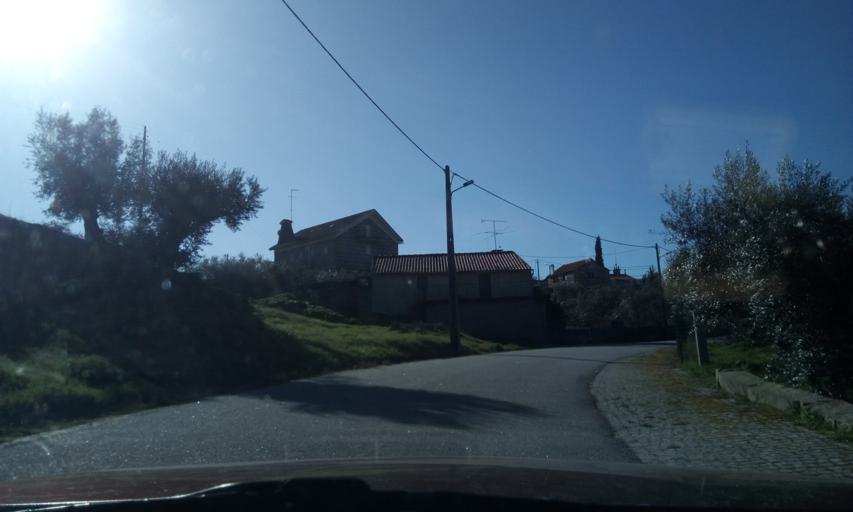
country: PT
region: Guarda
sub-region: Celorico da Beira
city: Celorico da Beira
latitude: 40.6904
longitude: -7.4441
